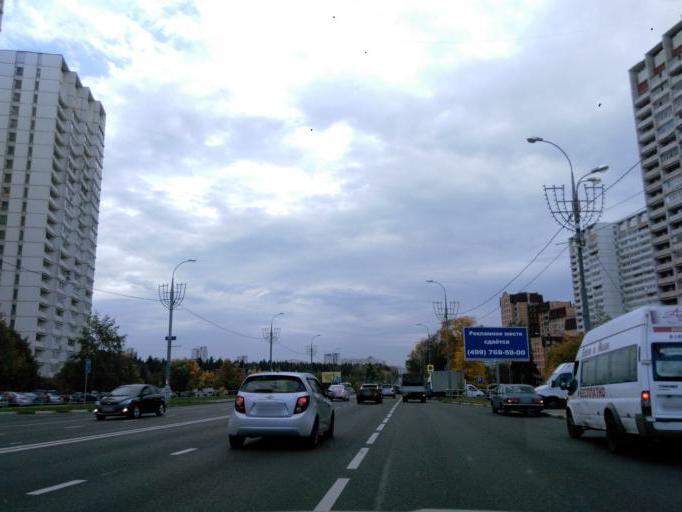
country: RU
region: Moscow
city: Zelenograd
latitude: 55.9948
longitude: 37.1891
